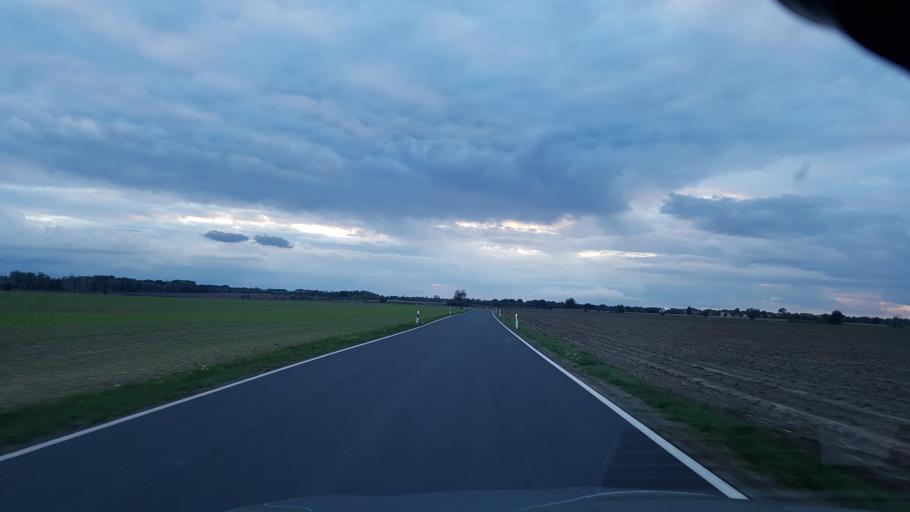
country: DE
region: Saxony
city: Grossenhain
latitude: 51.3245
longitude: 13.5759
